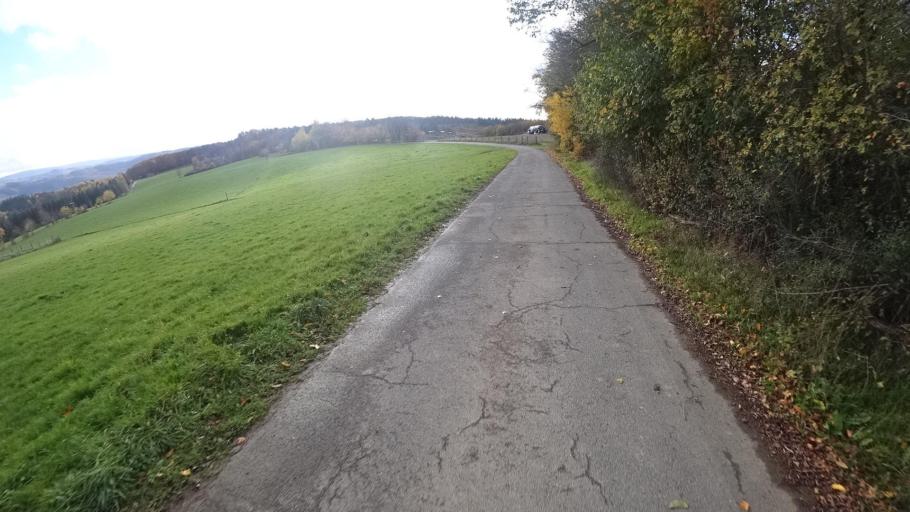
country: DE
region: Rheinland-Pfalz
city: Lind
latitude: 50.4896
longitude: 6.9354
